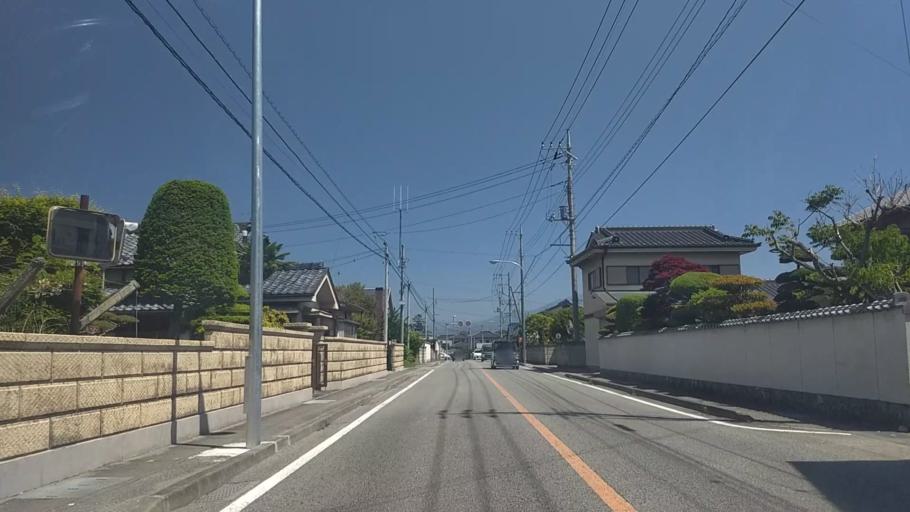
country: JP
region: Yamanashi
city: Ryuo
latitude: 35.6526
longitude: 138.4636
